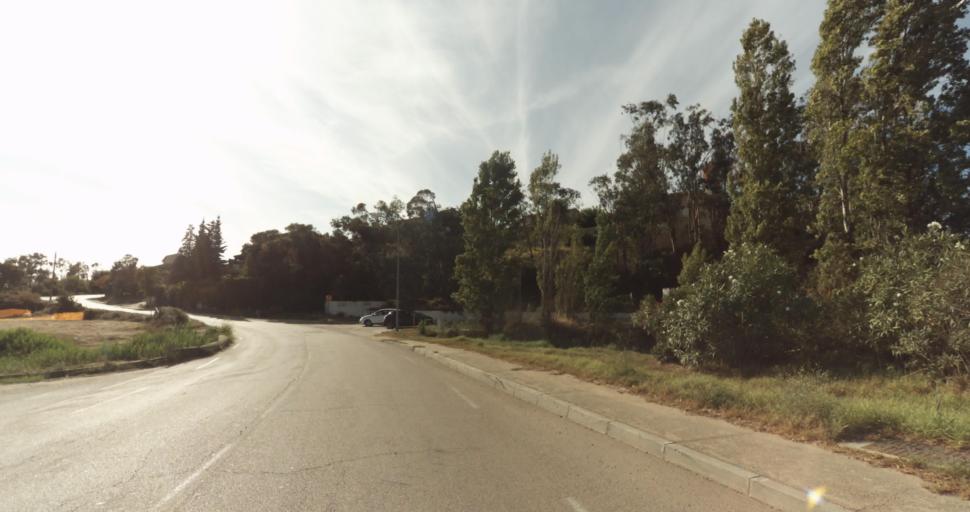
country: FR
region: Corsica
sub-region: Departement de la Corse-du-Sud
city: Ajaccio
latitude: 41.9307
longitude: 8.7848
